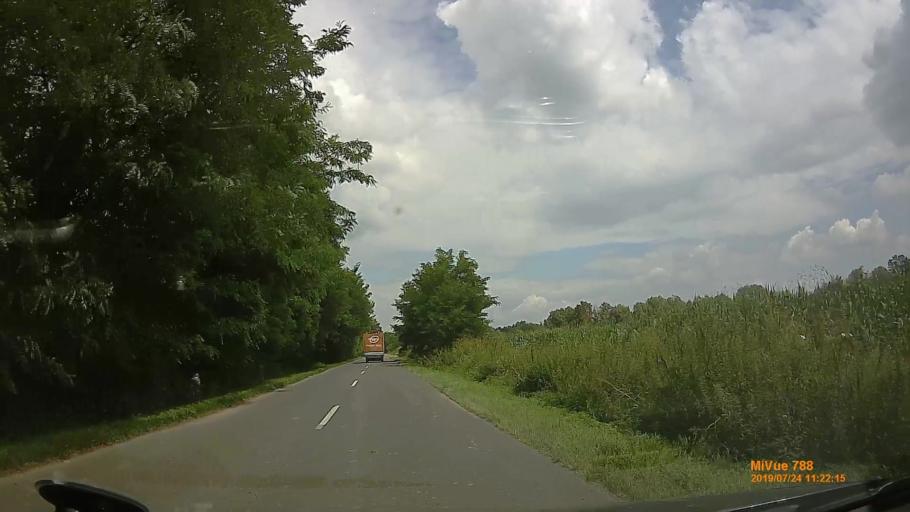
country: HU
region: Szabolcs-Szatmar-Bereg
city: Tarpa
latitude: 48.1741
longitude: 22.4621
